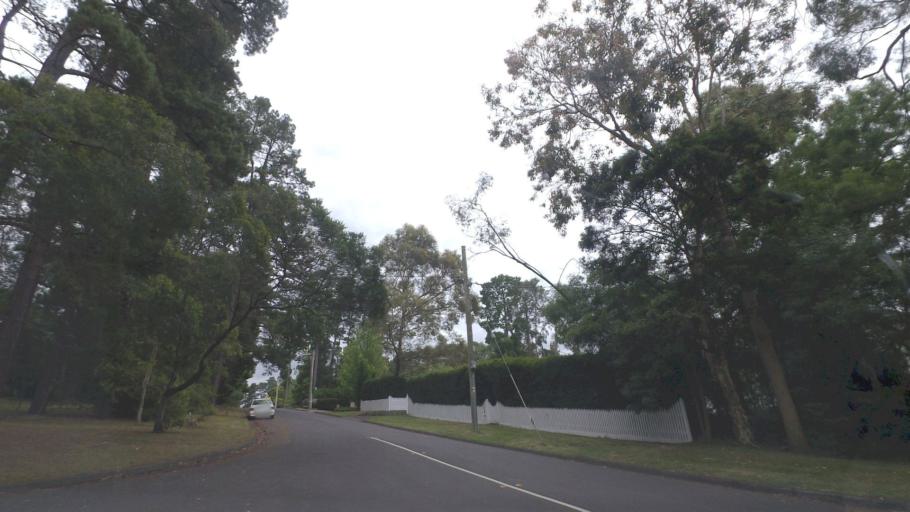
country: AU
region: Victoria
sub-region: Manningham
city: Park Orchards
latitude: -37.7821
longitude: 145.2201
